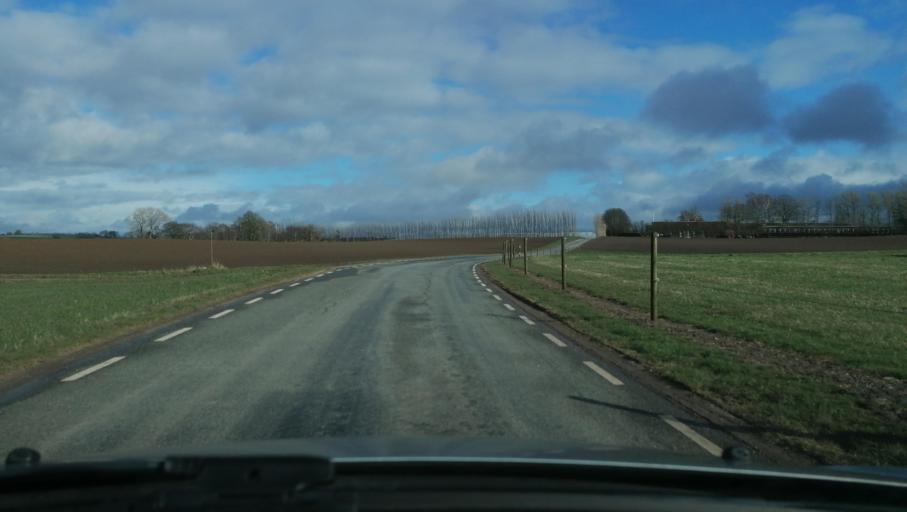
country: DK
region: Zealand
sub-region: Odsherred Kommune
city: Horve
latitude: 55.7547
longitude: 11.3874
